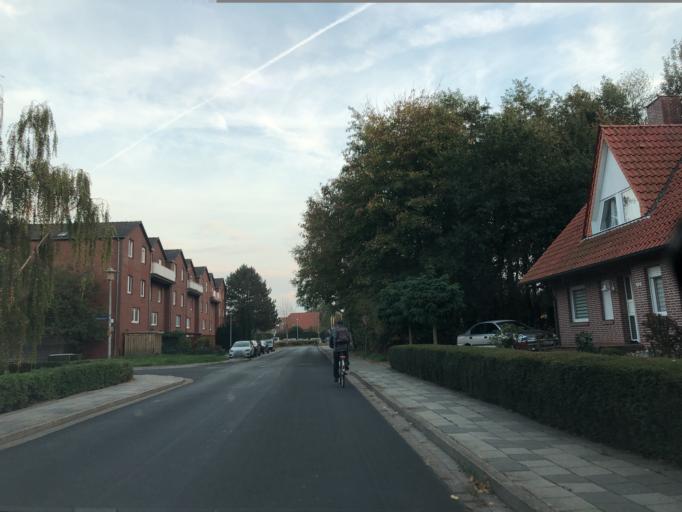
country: DE
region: Lower Saxony
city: Papenburg
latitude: 53.0733
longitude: 7.4380
